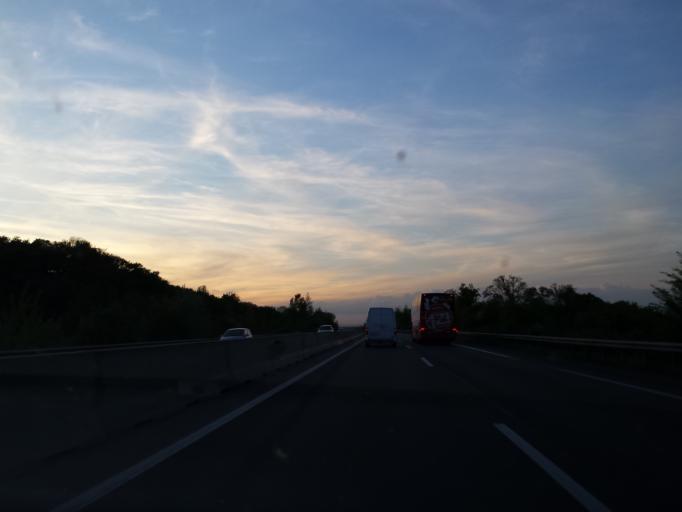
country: AT
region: Lower Austria
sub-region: Politischer Bezirk Ganserndorf
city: Orth an der Donau
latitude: 48.0853
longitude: 16.6727
